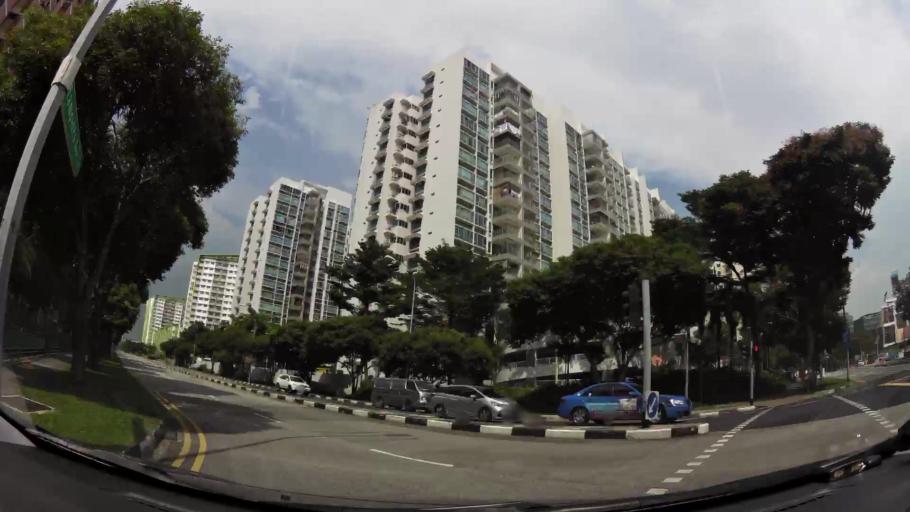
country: SG
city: Singapore
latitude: 1.3560
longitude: 103.9380
